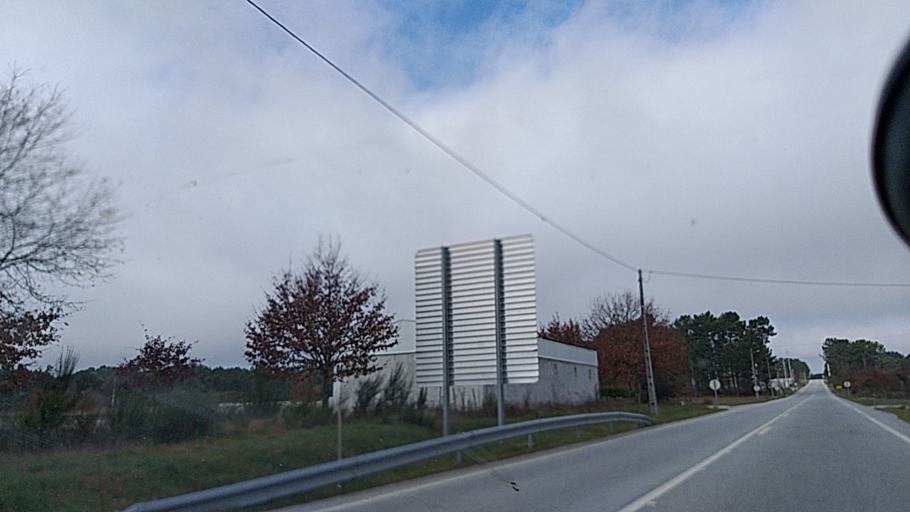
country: PT
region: Guarda
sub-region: Aguiar da Beira
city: Aguiar da Beira
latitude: 40.7908
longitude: -7.5086
